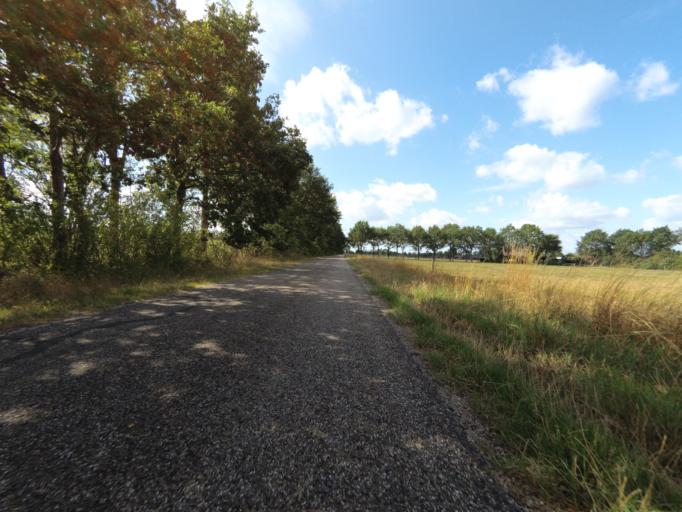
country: NL
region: Overijssel
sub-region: Gemeente Haaksbergen
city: Haaksbergen
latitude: 52.1384
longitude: 6.7642
